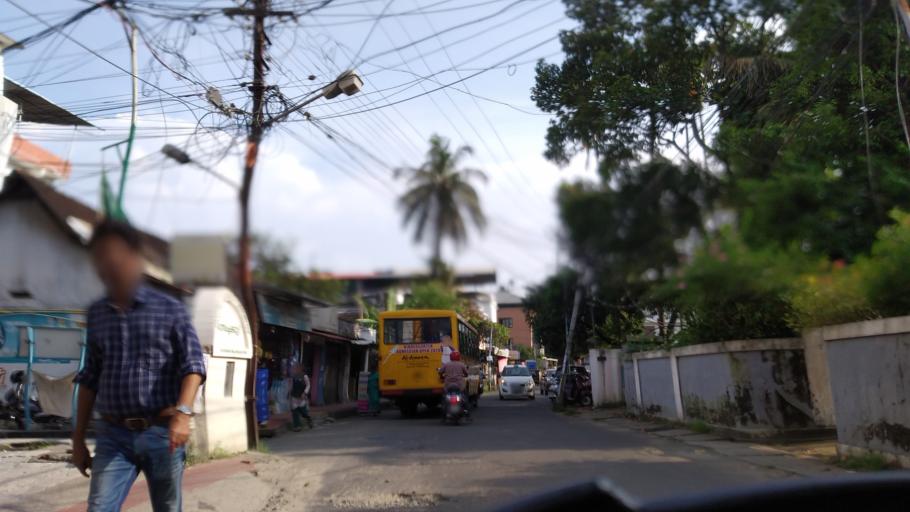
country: IN
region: Kerala
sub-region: Ernakulam
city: Cochin
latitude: 9.9963
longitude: 76.2865
